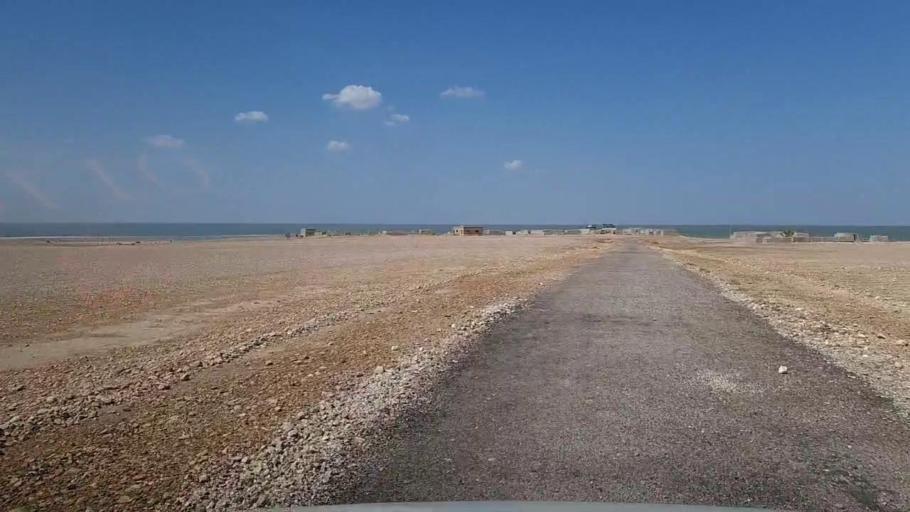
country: PK
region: Sindh
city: Bhan
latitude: 26.3850
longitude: 67.6299
